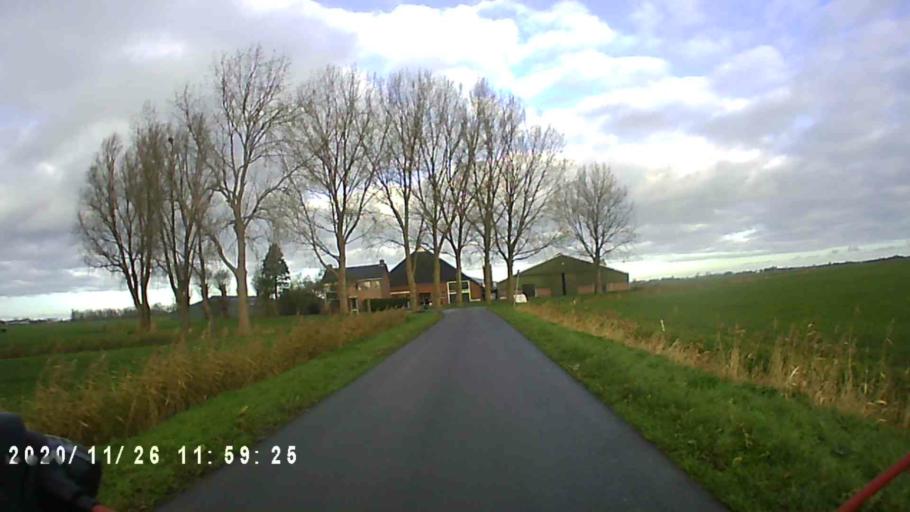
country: NL
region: Groningen
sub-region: Gemeente Bedum
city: Bedum
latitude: 53.3160
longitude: 6.6045
